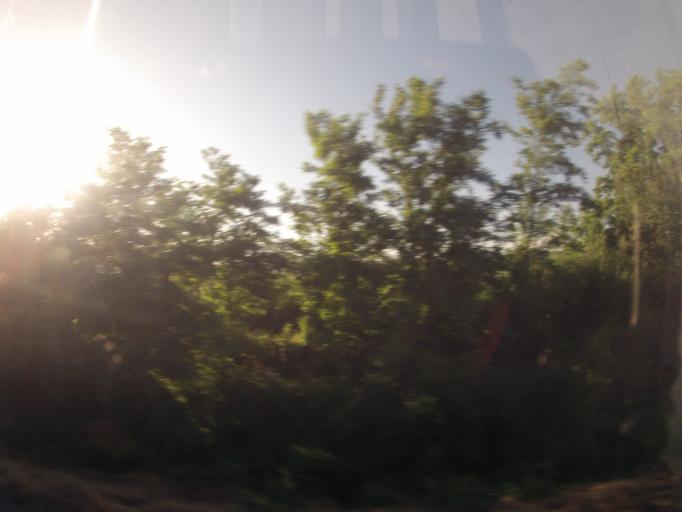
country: CL
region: O'Higgins
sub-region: Provincia de Colchagua
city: Chimbarongo
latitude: -34.6726
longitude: -71.0016
